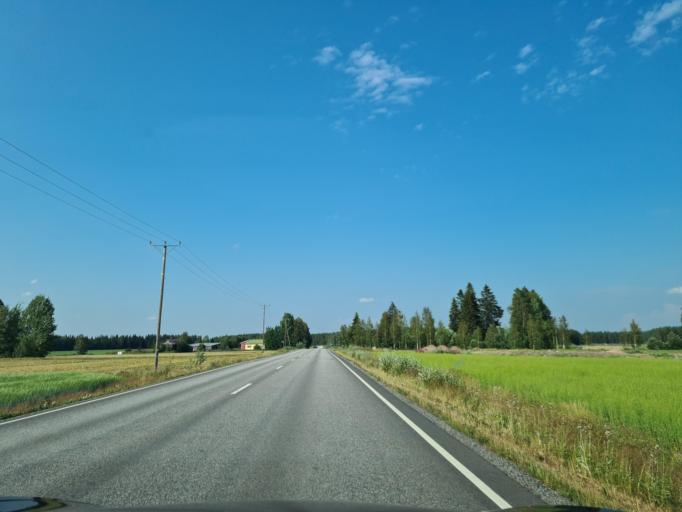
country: FI
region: Satakunta
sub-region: Pohjois-Satakunta
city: Kankaanpaeae
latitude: 61.9154
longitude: 22.5038
